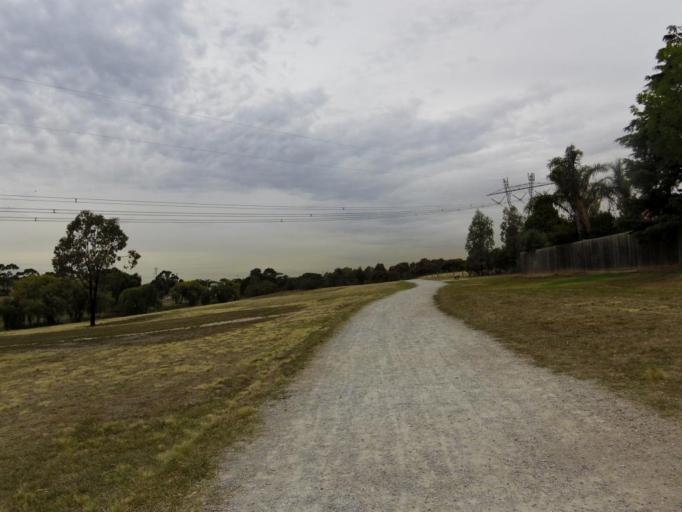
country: AU
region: Victoria
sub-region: Brimbank
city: Keilor Lodge
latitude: -37.7043
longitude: 144.7984
